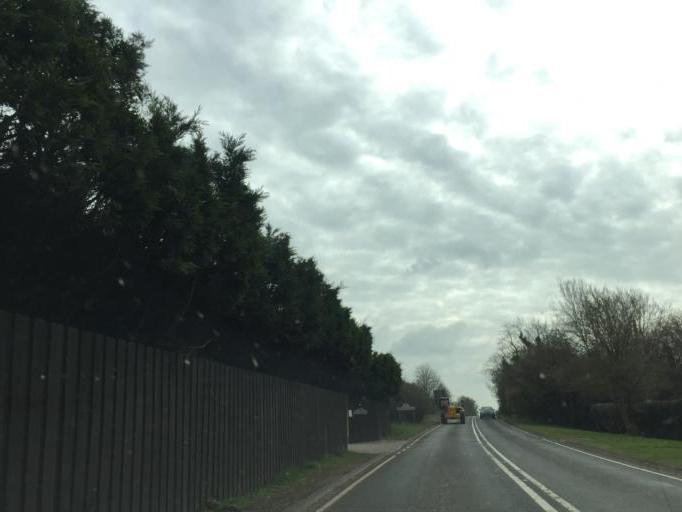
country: GB
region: England
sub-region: Warwickshire
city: Henley in Arden
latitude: 52.2901
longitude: -1.7976
